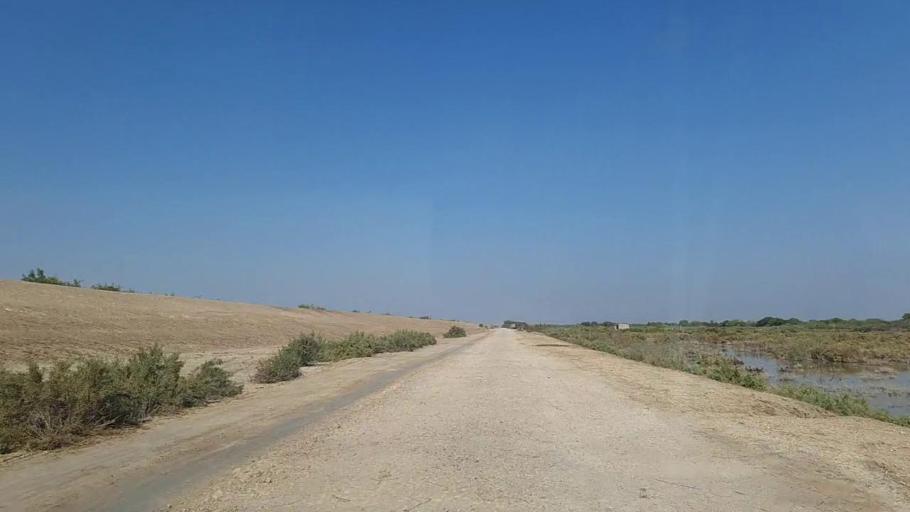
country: PK
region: Sindh
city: Chuhar Jamali
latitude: 24.4576
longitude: 68.0008
